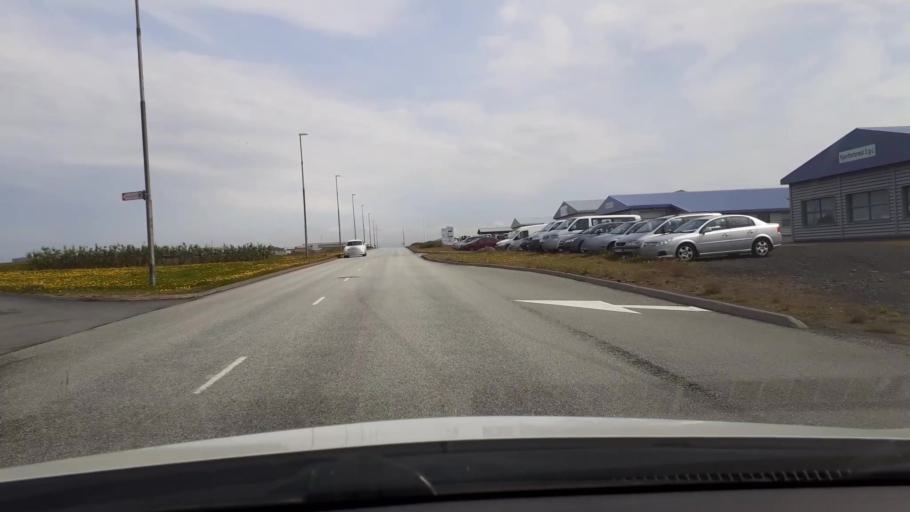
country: IS
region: Southern Peninsula
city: Reykjanesbaer
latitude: 63.9720
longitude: -22.5295
